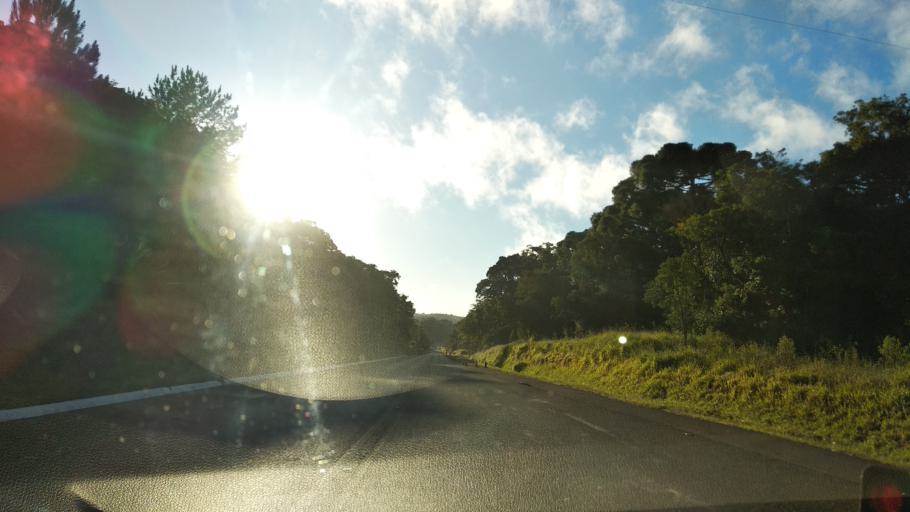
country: BR
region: Santa Catarina
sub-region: Correia Pinto
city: Correia Pinto
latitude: -27.6144
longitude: -50.7156
